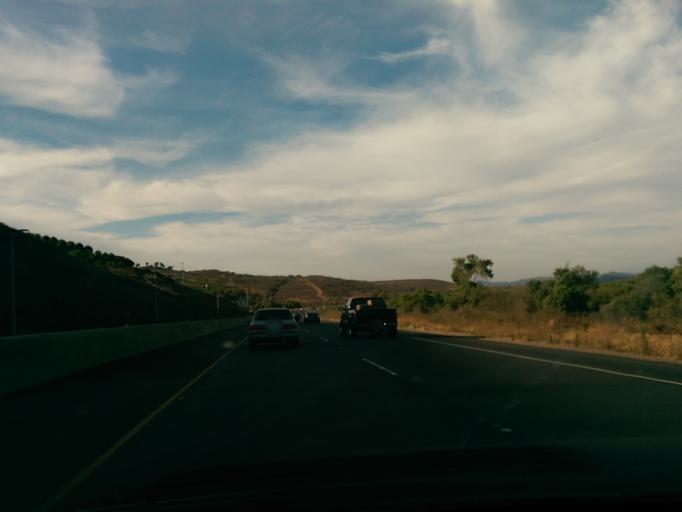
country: US
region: California
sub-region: San Diego County
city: Bonsall
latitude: 33.2694
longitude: -117.2365
